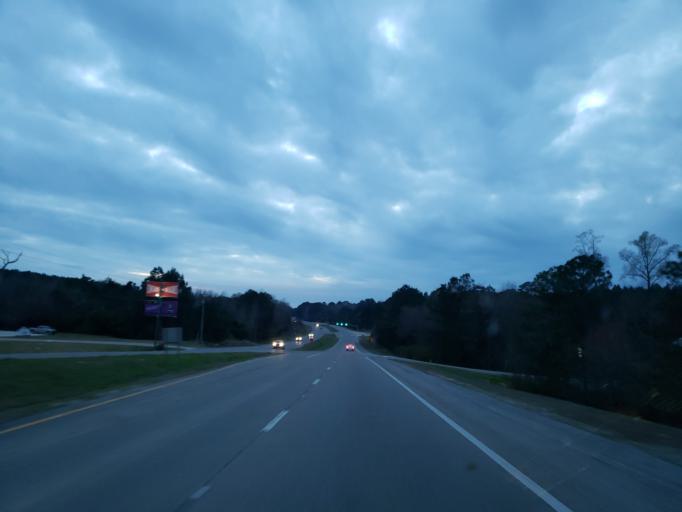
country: US
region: Mississippi
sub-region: Lauderdale County
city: Marion
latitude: 32.3671
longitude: -88.6489
